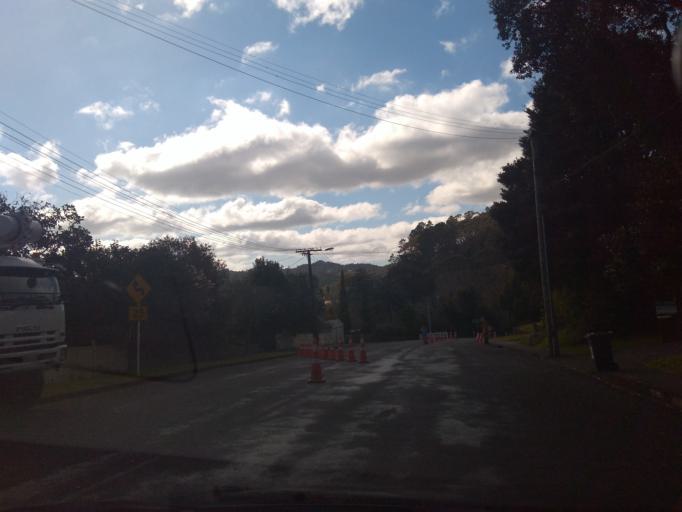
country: NZ
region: Northland
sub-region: Whangarei
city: Whangarei
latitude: -35.7028
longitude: 174.3280
